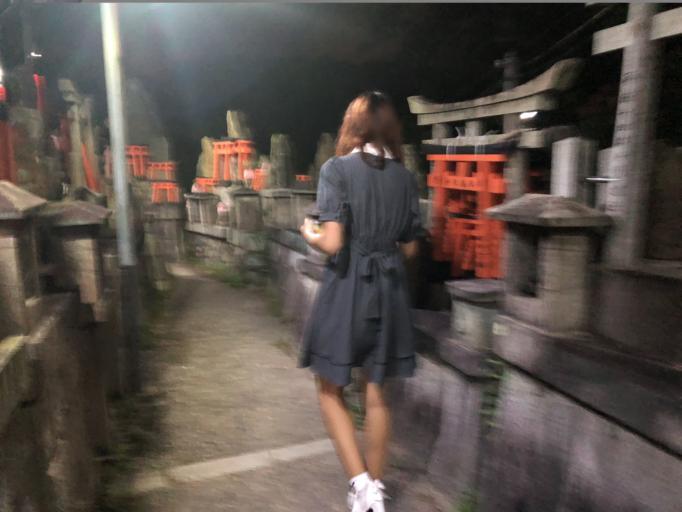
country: JP
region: Kyoto
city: Kyoto
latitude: 34.9696
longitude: 135.7816
